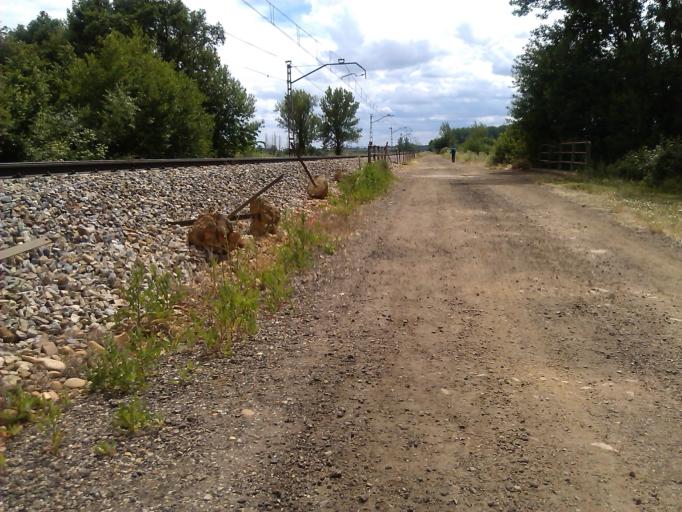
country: ES
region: Castille and Leon
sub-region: Provincia de Leon
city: Hospital de Orbigo
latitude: 42.4607
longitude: -5.8446
